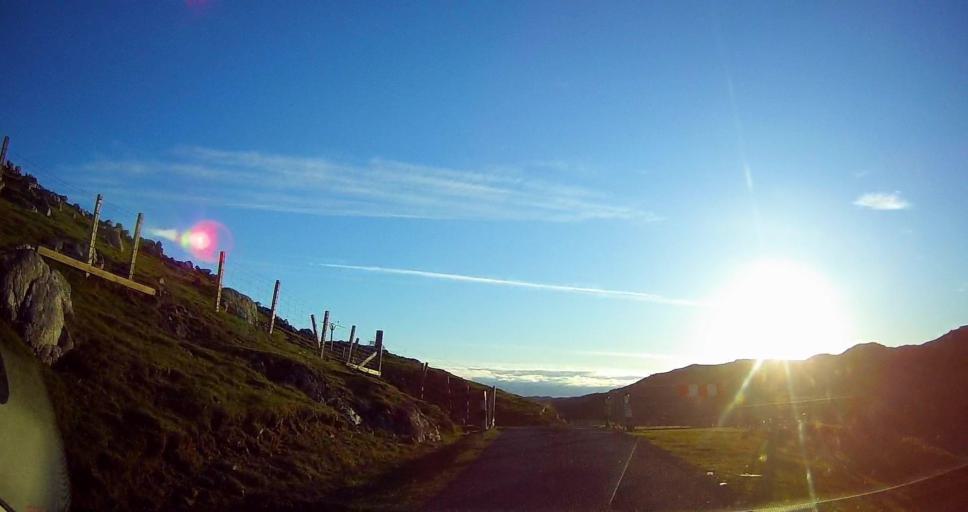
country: GB
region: Scotland
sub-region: Shetland Islands
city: Lerwick
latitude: 60.4488
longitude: -1.4224
